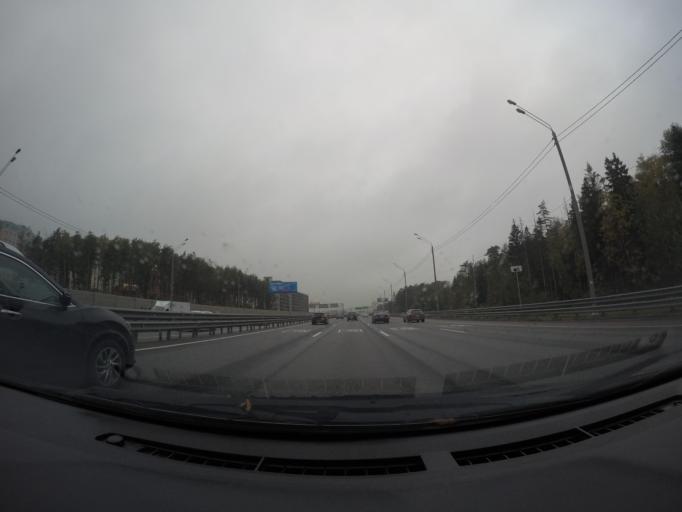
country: RU
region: Moskovskaya
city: Petrovo-Dal'neye
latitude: 55.7756
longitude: 37.2204
